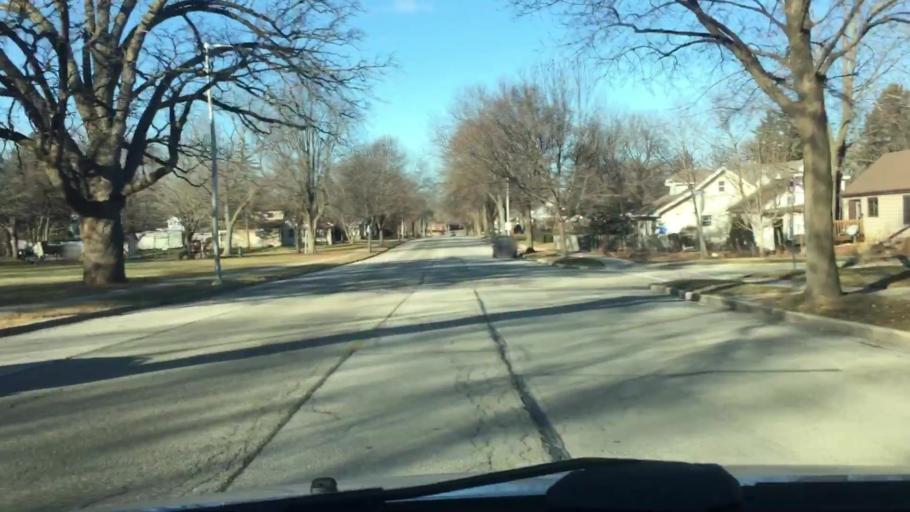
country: US
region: Wisconsin
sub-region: Waukesha County
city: Pewaukee
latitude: 43.0786
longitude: -88.2568
